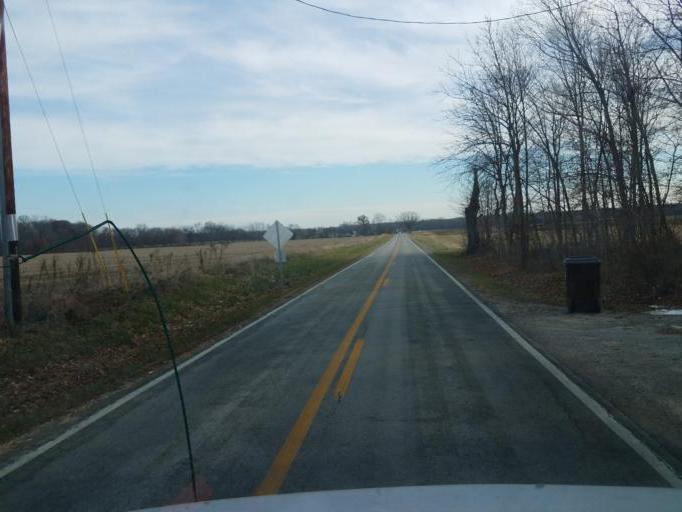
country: US
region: Ohio
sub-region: Delaware County
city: Ashley
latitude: 40.3445
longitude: -82.9654
